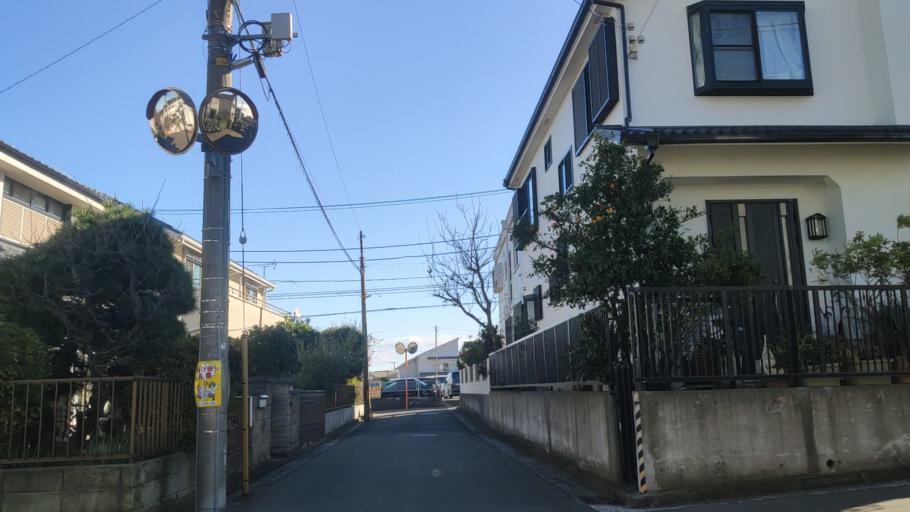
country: JP
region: Kanagawa
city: Yokohama
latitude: 35.4218
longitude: 139.6449
